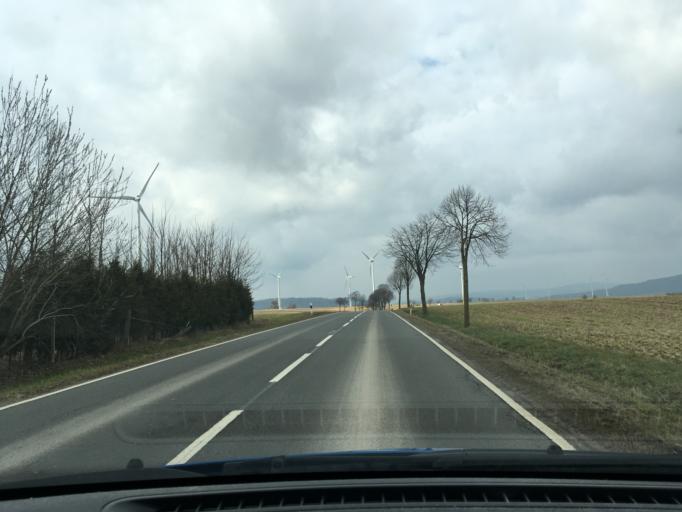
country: DE
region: Lower Saxony
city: Dransfeld
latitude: 51.5066
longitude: 9.7522
